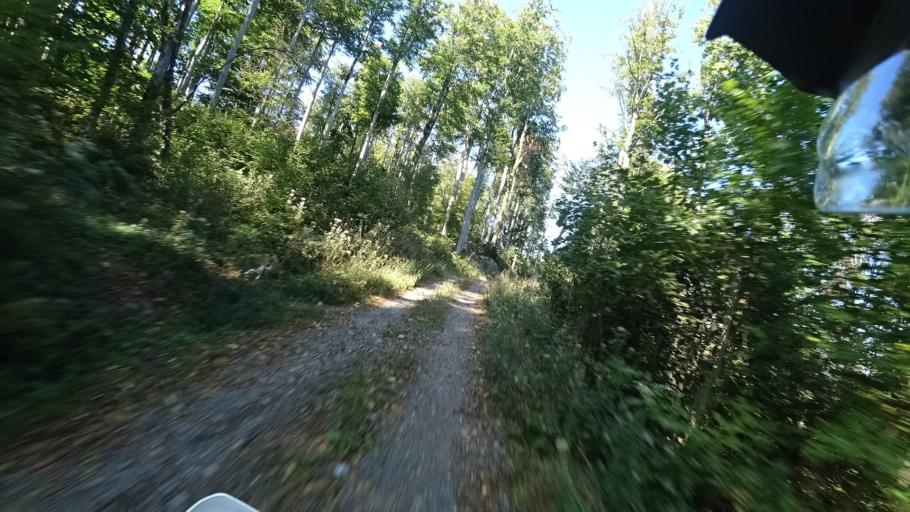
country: HR
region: Primorsko-Goranska
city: Vrbovsko
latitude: 45.2932
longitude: 15.1302
